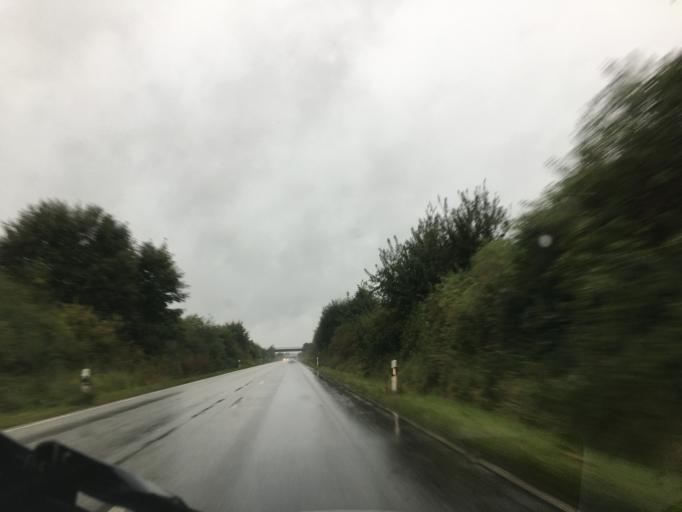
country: DE
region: Schleswig-Holstein
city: Brodersdorf
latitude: 54.3751
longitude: 10.2407
